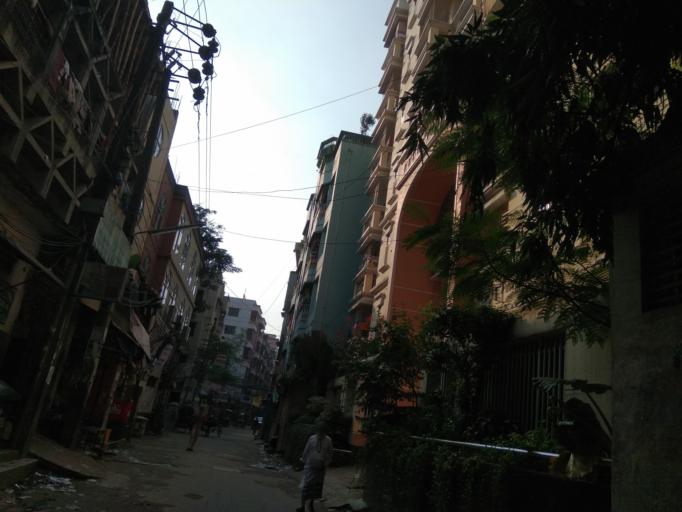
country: BD
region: Dhaka
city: Azimpur
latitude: 23.7609
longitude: 90.3574
